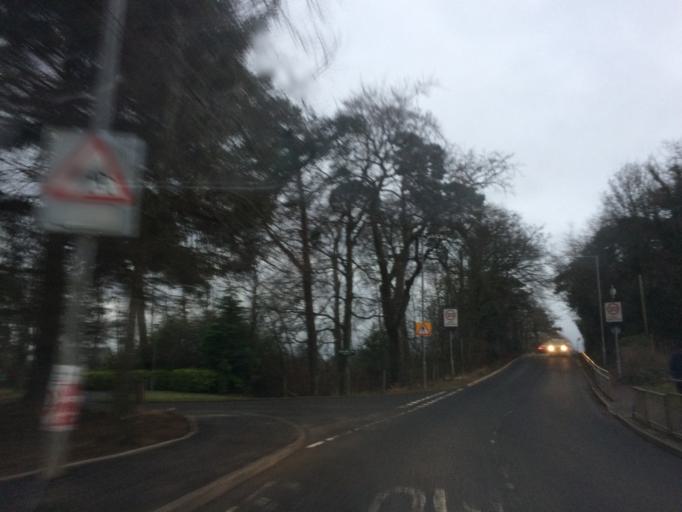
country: GB
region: Scotland
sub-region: East Renfrewshire
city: Newton Mearns
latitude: 55.7891
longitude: -4.3307
